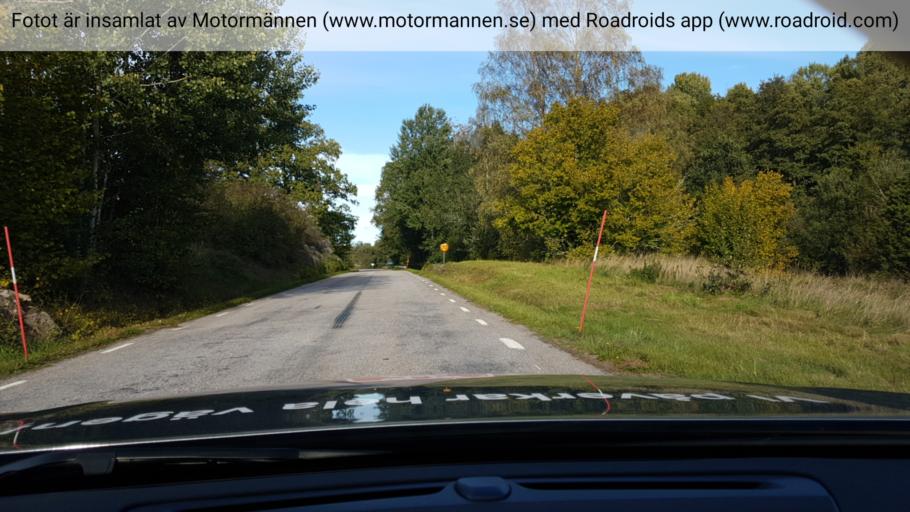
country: SE
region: OEstergoetland
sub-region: Valdemarsviks Kommun
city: Valdemarsvik
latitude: 58.0430
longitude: 16.5998
